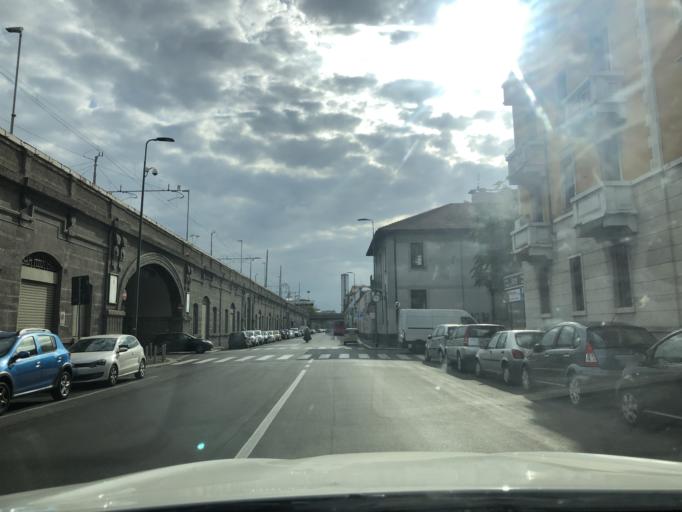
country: IT
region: Lombardy
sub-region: Citta metropolitana di Milano
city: Milano
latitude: 45.4945
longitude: 9.2111
